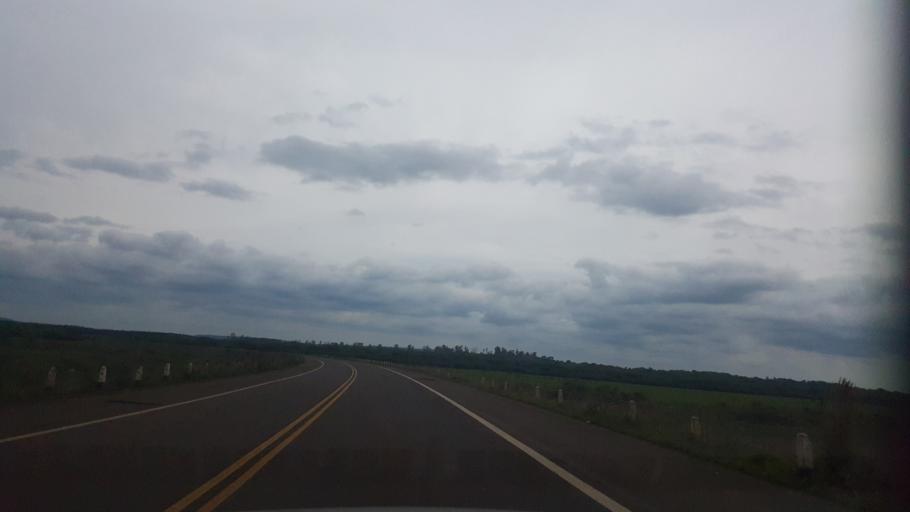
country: AR
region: Misiones
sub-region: Departamento de Candelaria
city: Candelaria
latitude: -27.4825
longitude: -55.7469
